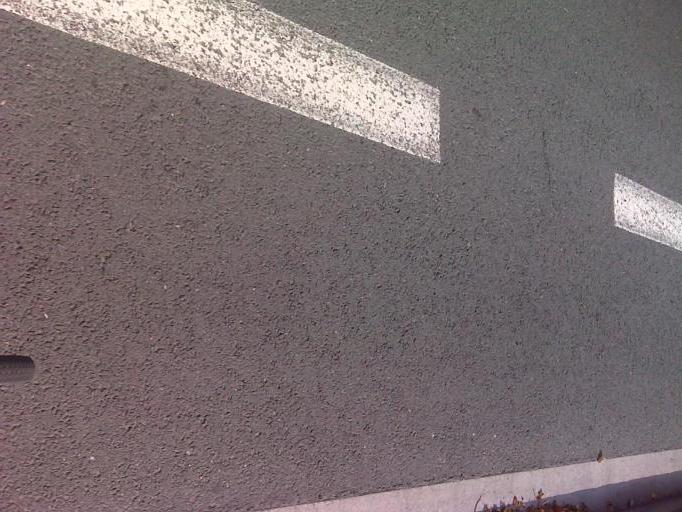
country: FR
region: Poitou-Charentes
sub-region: Departement de la Charente-Maritime
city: Rochefort
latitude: 45.9302
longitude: -0.9594
